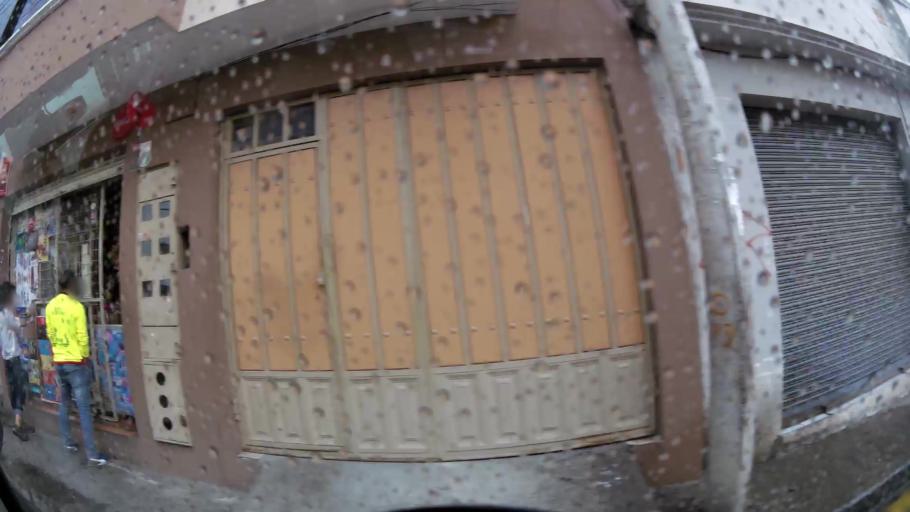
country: EC
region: Azuay
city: Cuenca
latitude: -2.8966
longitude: -79.0240
